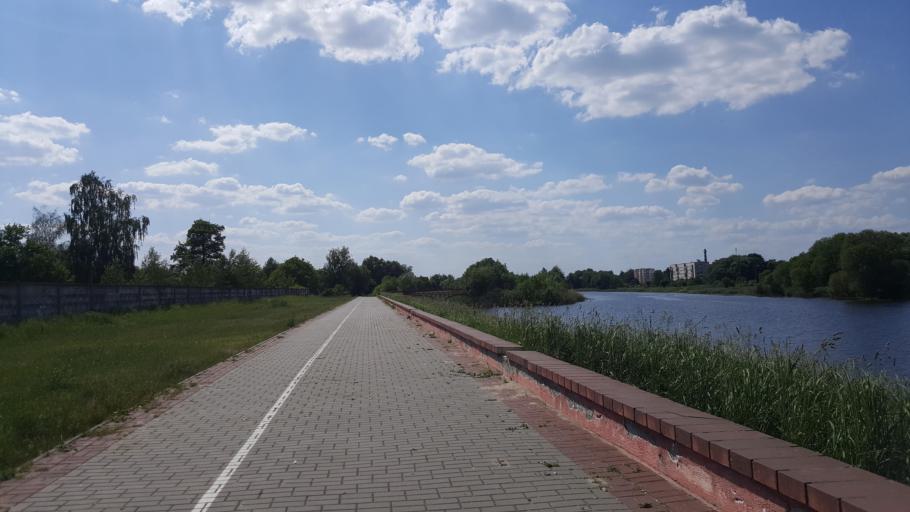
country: BY
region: Brest
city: Kobryn
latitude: 52.2159
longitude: 24.3563
